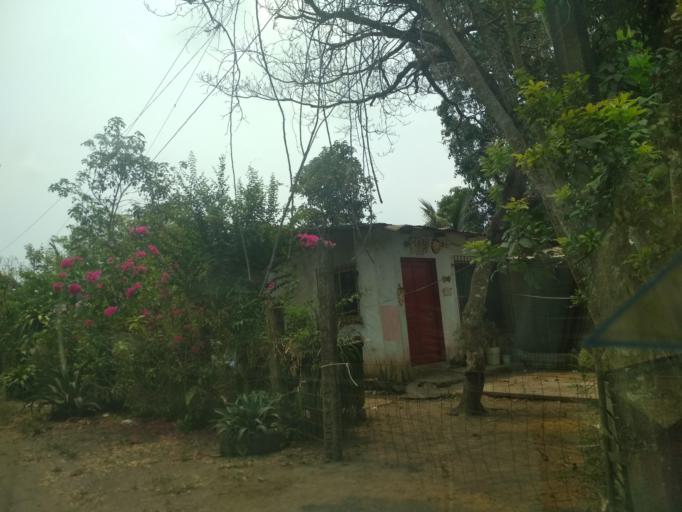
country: MX
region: Veracruz
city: Paso del Toro
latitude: 19.0518
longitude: -96.1526
